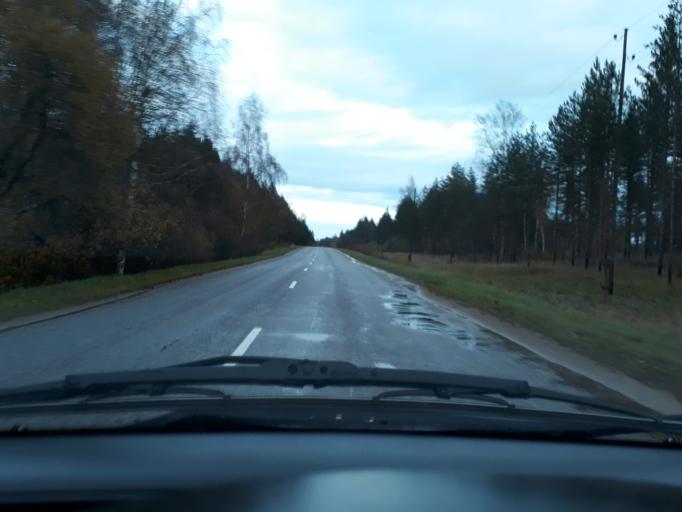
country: LV
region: Dobeles Rajons
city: Dobele
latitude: 56.6032
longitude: 23.2017
